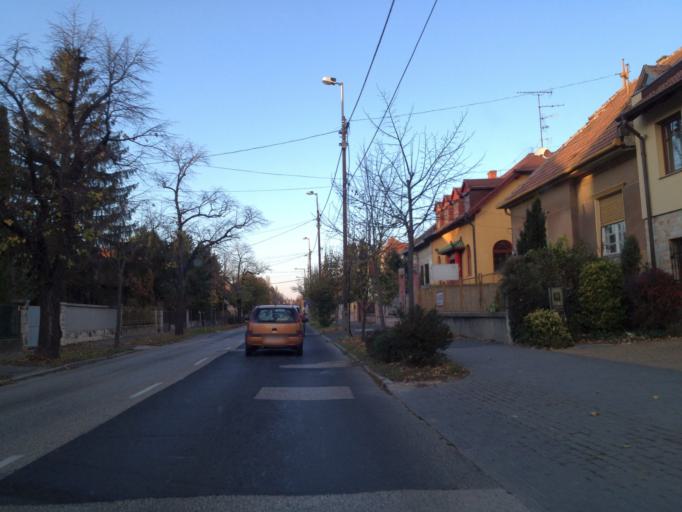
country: HU
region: Gyor-Moson-Sopron
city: Gyor
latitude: 47.6725
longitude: 17.6417
